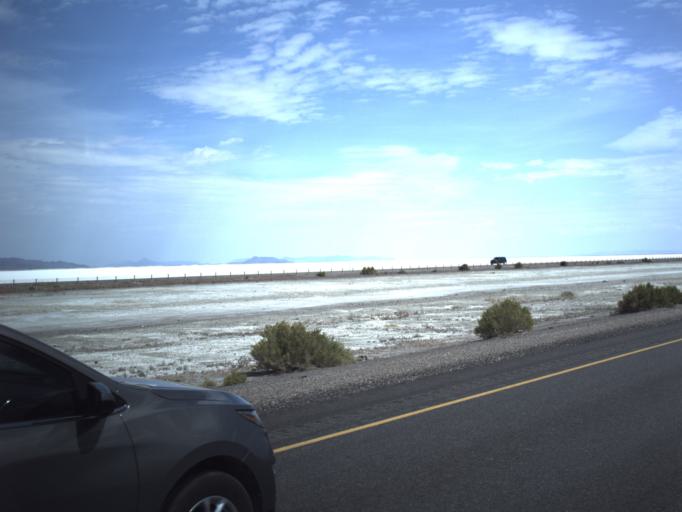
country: US
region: Utah
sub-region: Tooele County
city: Wendover
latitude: 40.7396
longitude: -113.9064
